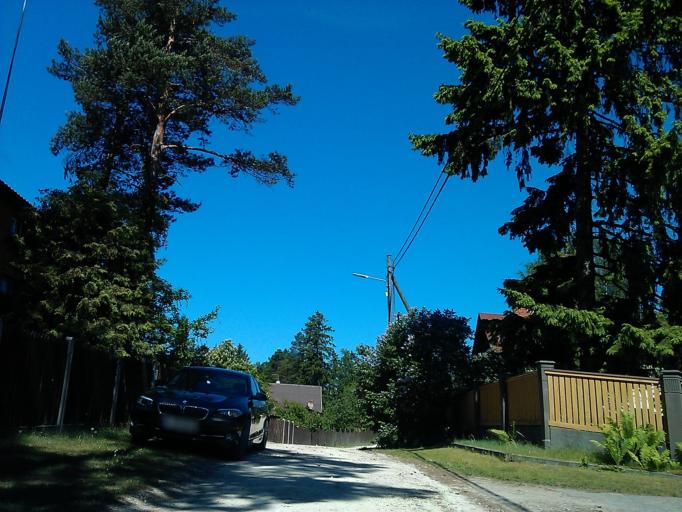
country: LV
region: Riga
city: Bergi
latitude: 57.0065
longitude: 24.3326
